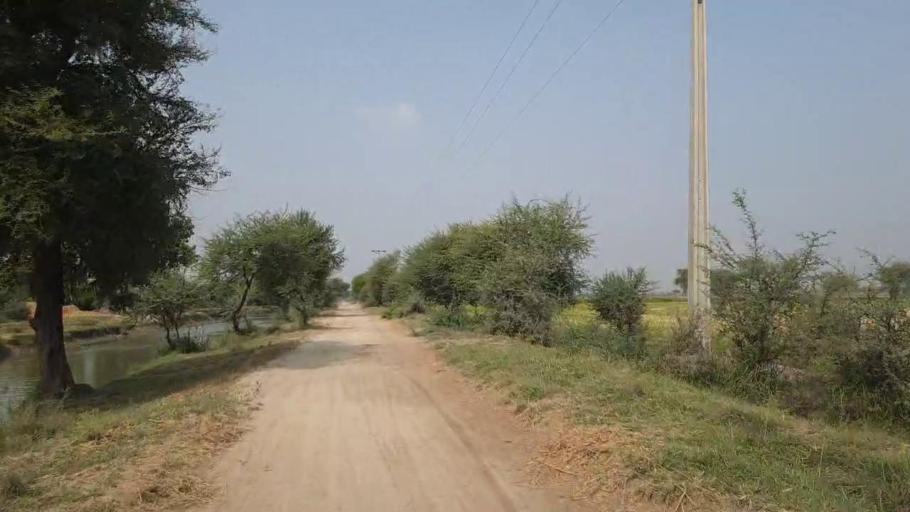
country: PK
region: Sindh
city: Kario
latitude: 24.8378
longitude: 68.5413
